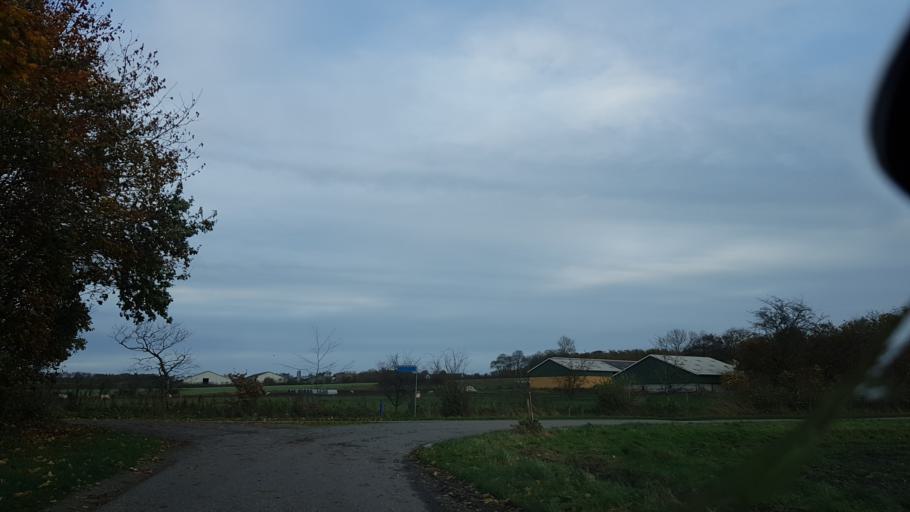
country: DK
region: South Denmark
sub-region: Haderslev Kommune
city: Vojens
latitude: 55.2509
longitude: 9.1863
